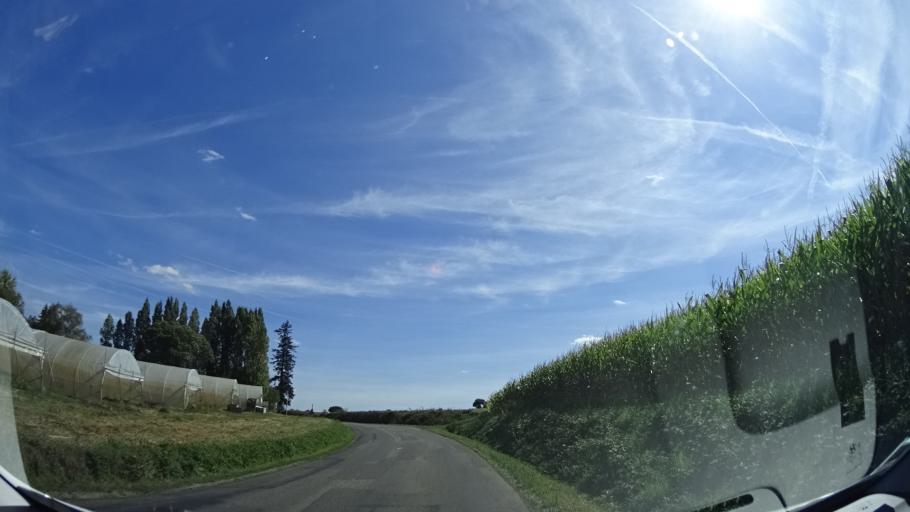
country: FR
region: Brittany
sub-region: Departement d'Ille-et-Vilaine
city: Geveze
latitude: 48.2247
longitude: -1.7727
